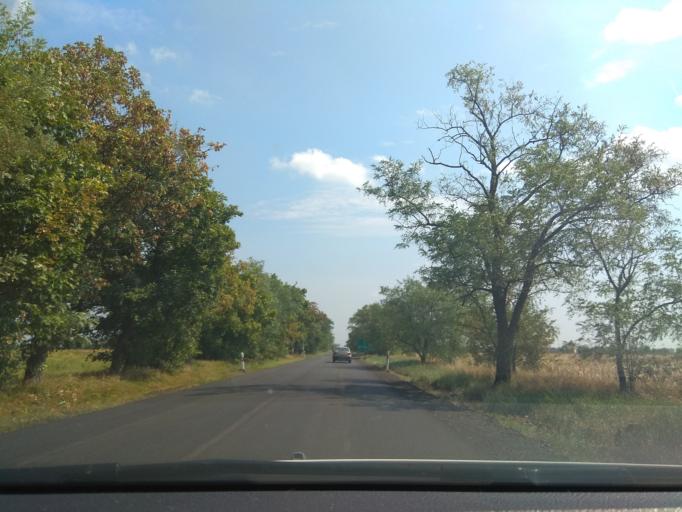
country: HU
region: Borsod-Abauj-Zemplen
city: Mezokovesd
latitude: 47.8116
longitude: 20.5376
